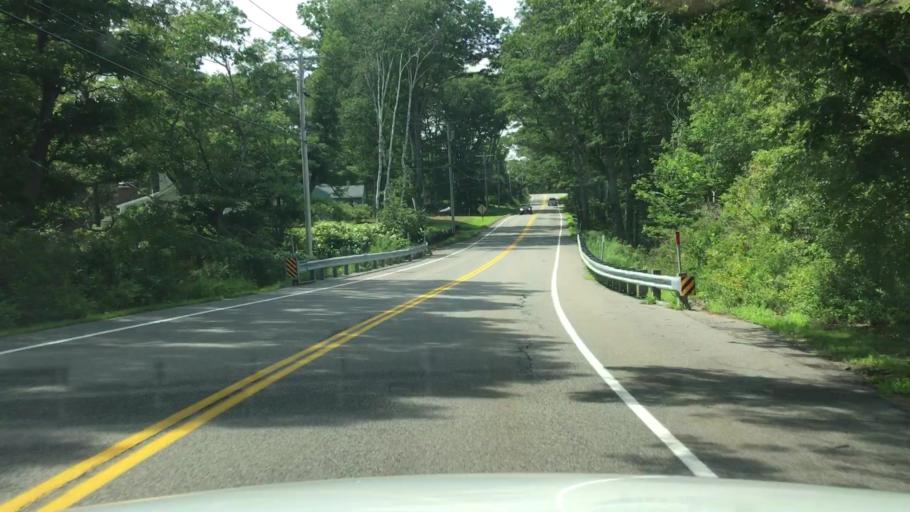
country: US
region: Maine
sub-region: Cumberland County
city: South Portland
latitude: 43.5809
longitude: -70.2485
